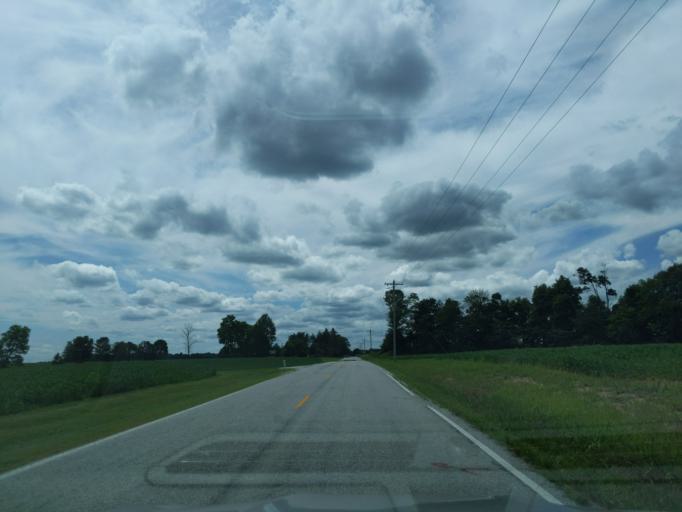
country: US
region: Indiana
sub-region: Ripley County
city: Batesville
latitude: 39.2379
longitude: -85.2616
